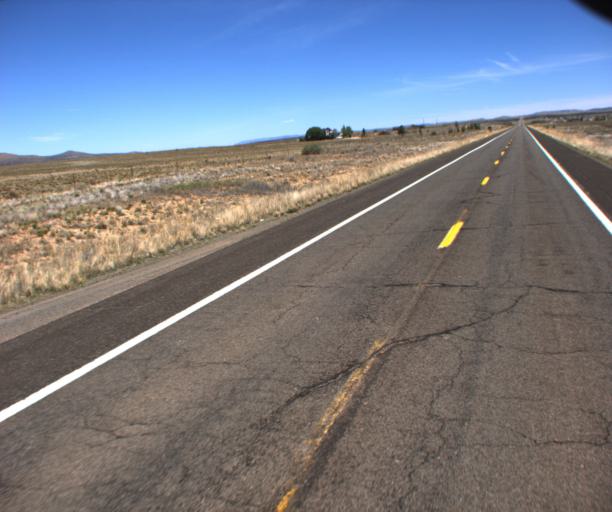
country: US
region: Arizona
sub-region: Mohave County
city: Peach Springs
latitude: 35.4770
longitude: -113.5796
